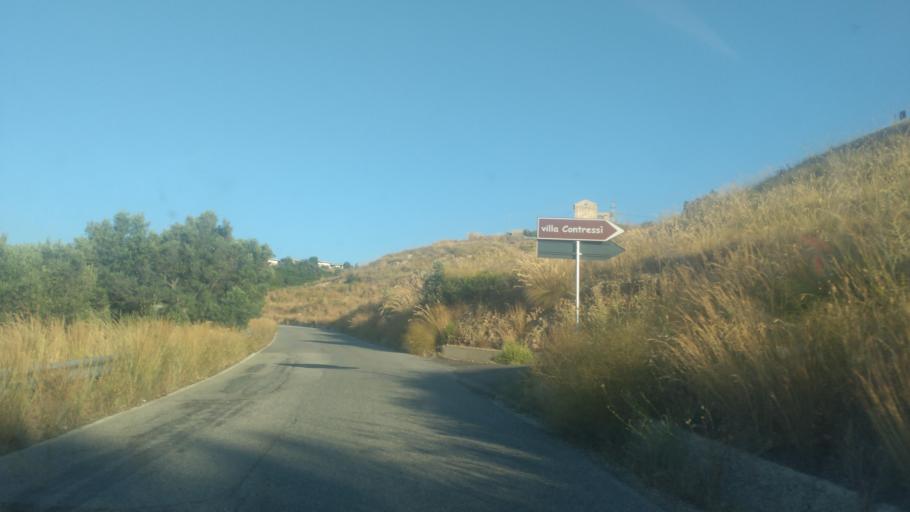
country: IT
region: Calabria
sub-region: Provincia di Catanzaro
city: Squillace Lido
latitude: 38.7592
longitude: 16.5632
